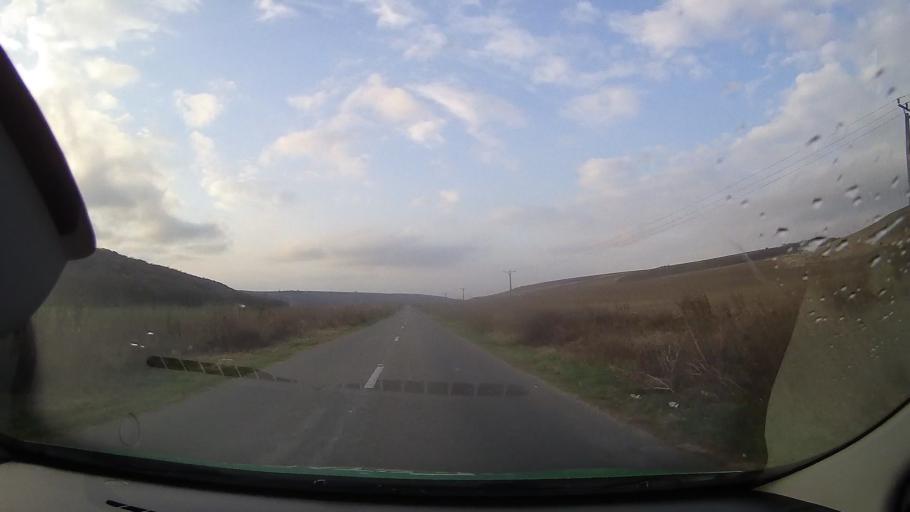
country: RO
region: Constanta
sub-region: Comuna Dobromir
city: Dobromir
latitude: 44.0307
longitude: 27.8591
